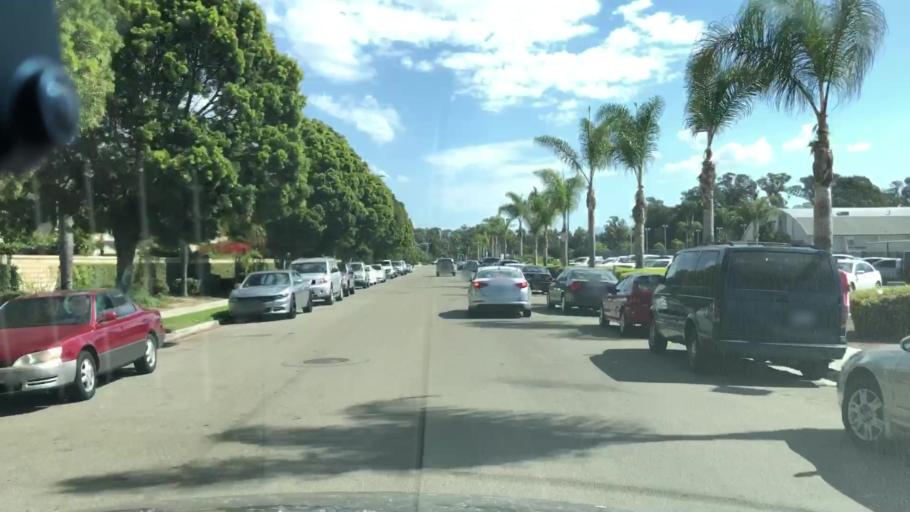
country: US
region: California
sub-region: Ventura County
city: Oxnard
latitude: 34.1717
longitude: -119.1629
